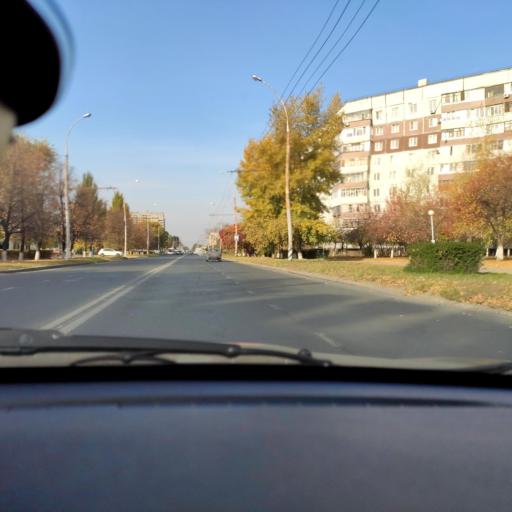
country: RU
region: Samara
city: Tol'yatti
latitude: 53.5345
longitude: 49.3192
